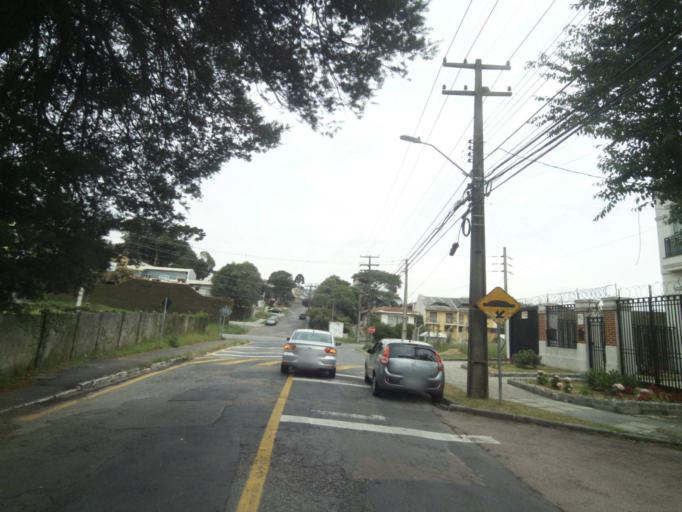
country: BR
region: Parana
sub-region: Curitiba
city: Curitiba
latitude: -25.4121
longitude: -49.3036
